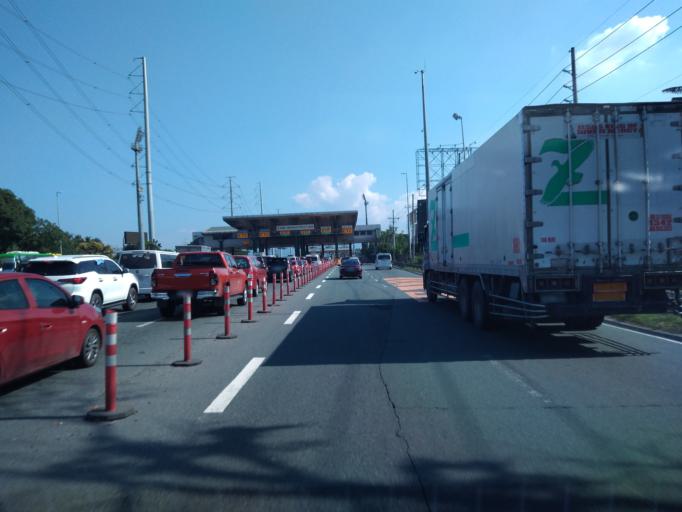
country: PH
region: Calabarzon
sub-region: Province of Laguna
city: Prinza
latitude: 14.2208
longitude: 121.1241
